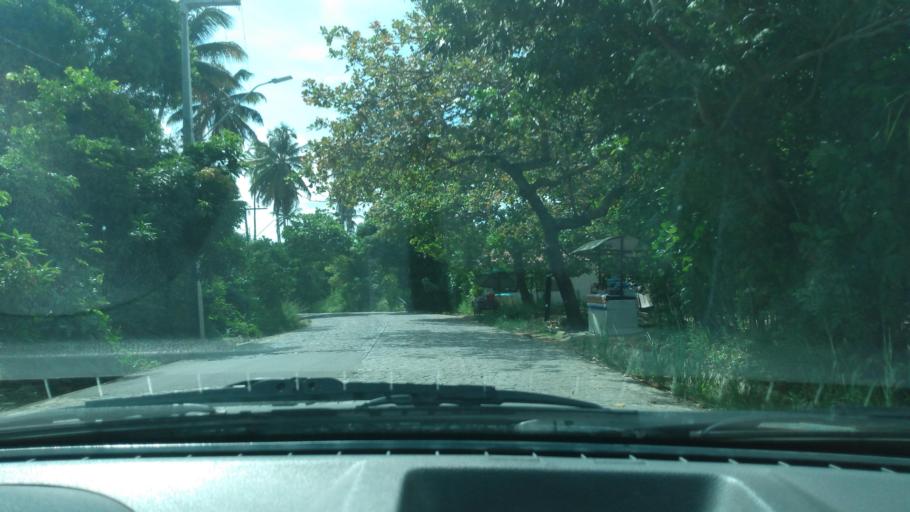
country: BR
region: Pernambuco
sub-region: Cabo De Santo Agostinho
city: Cabo
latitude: -8.3498
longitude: -34.9521
